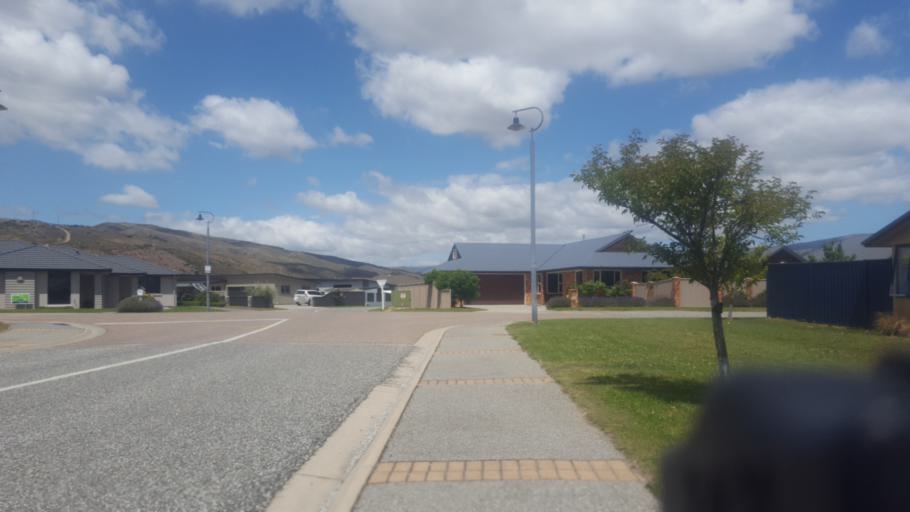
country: NZ
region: Otago
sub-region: Queenstown-Lakes District
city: Wanaka
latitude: -45.0490
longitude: 169.1990
